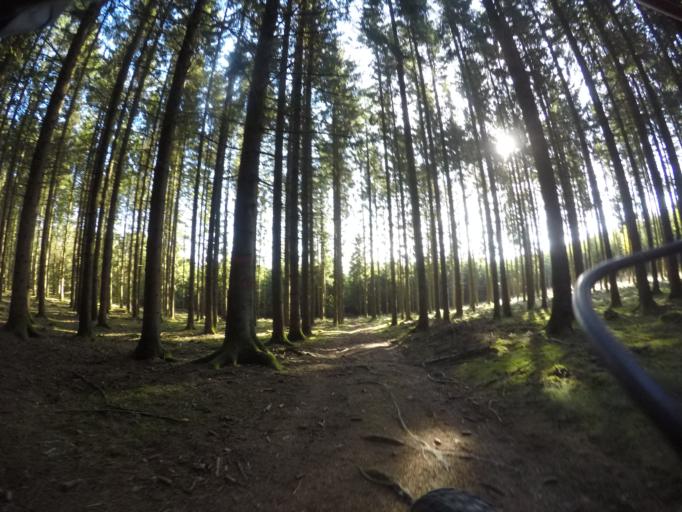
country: BE
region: Wallonia
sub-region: Province du Luxembourg
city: Fauvillers
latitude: 49.9030
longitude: 5.6703
